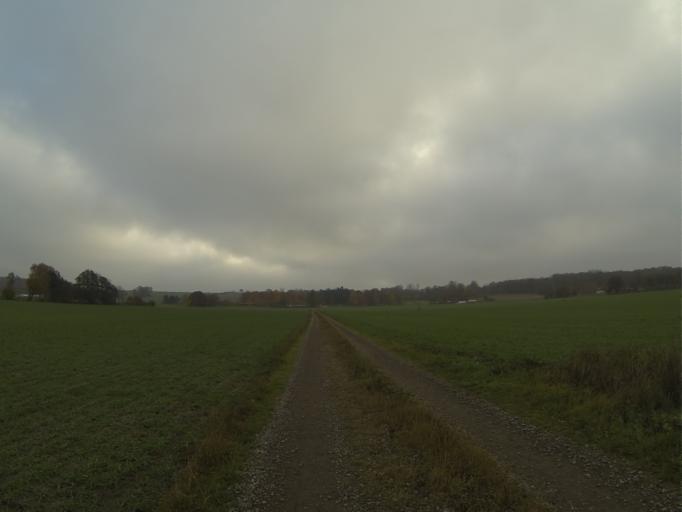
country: SE
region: Skane
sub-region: Lunds Kommun
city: Genarp
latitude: 55.7129
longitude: 13.3791
